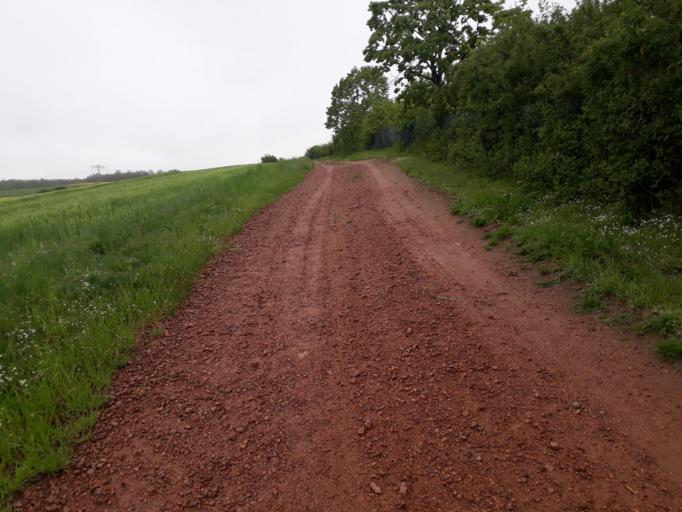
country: DE
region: Saxony
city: Reinhardtsgrimma
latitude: 50.8904
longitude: 13.7413
